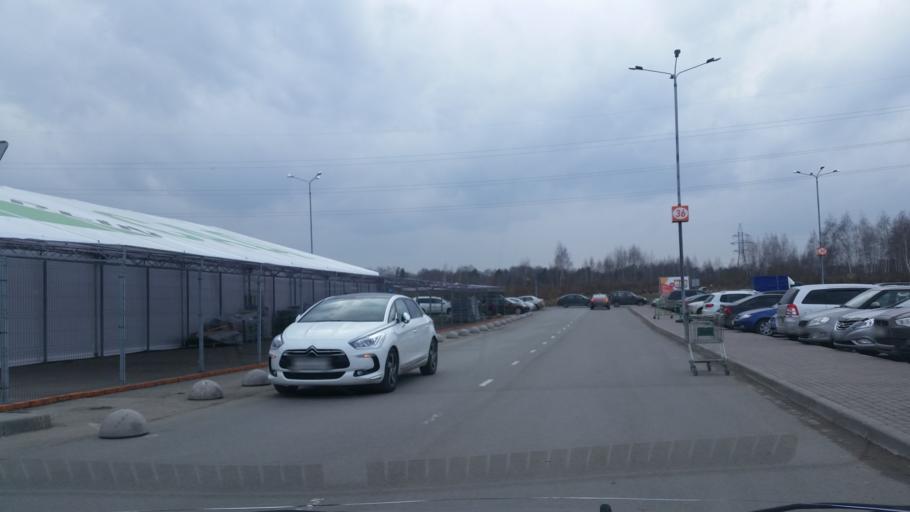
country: RU
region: Moskovskaya
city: Arkhangel'skoye
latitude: 55.8006
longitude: 37.2990
